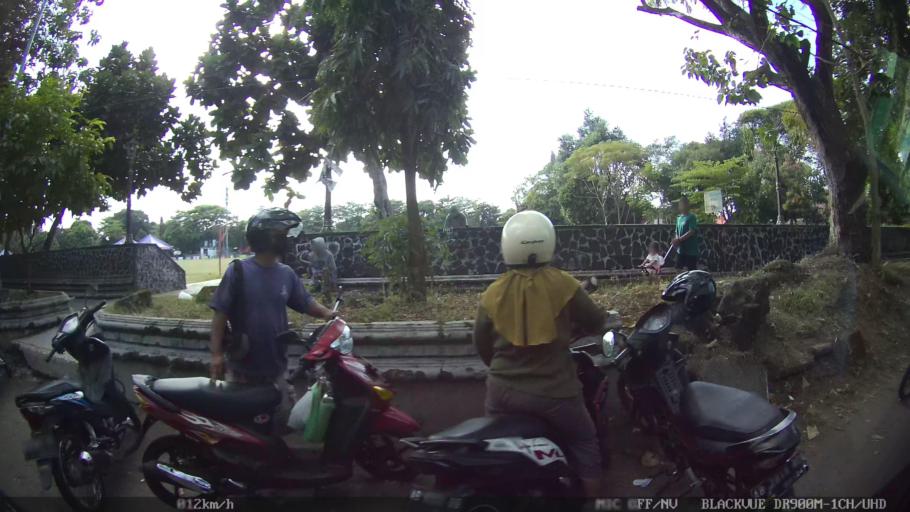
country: ID
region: Daerah Istimewa Yogyakarta
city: Kasihan
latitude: -7.8194
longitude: 110.3603
